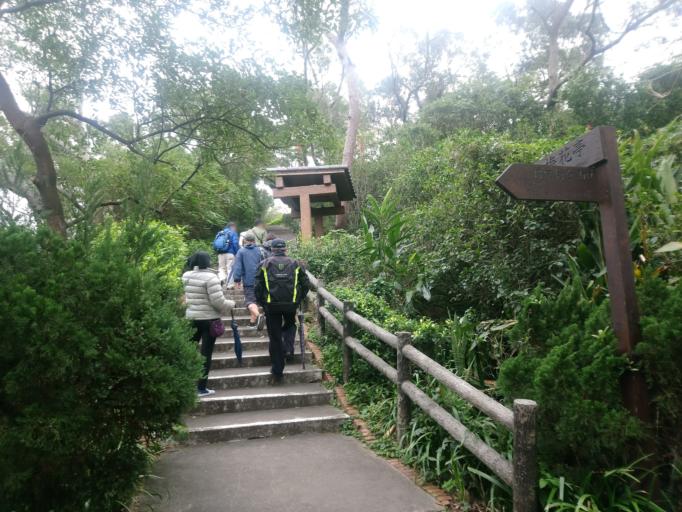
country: TW
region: Taiwan
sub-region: Hsinchu
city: Hsinchu
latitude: 24.7918
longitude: 120.9847
